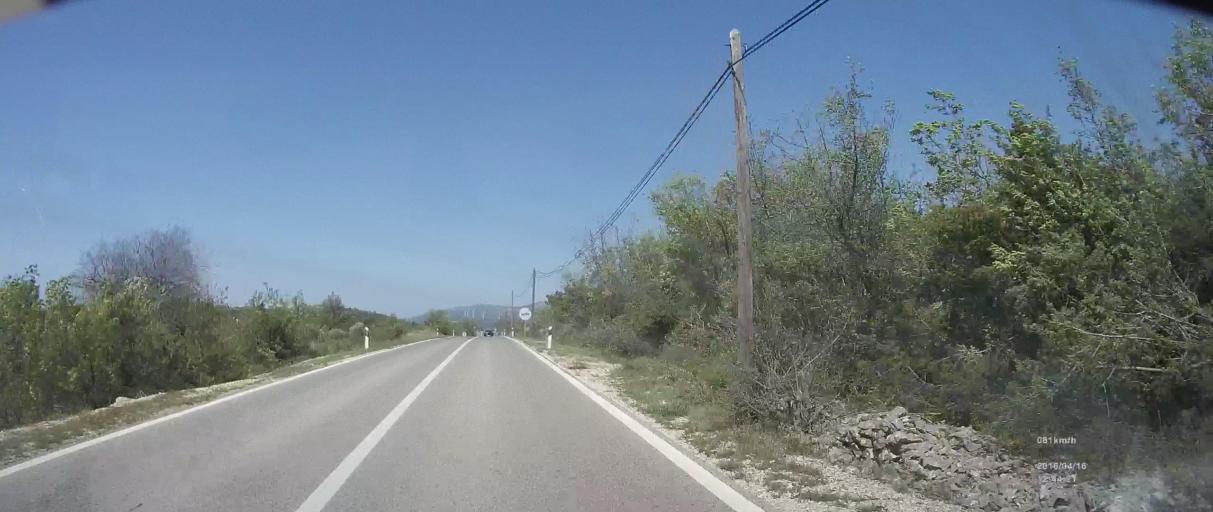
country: HR
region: Sibensko-Kniniska
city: Rogoznica
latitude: 43.6402
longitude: 16.0658
